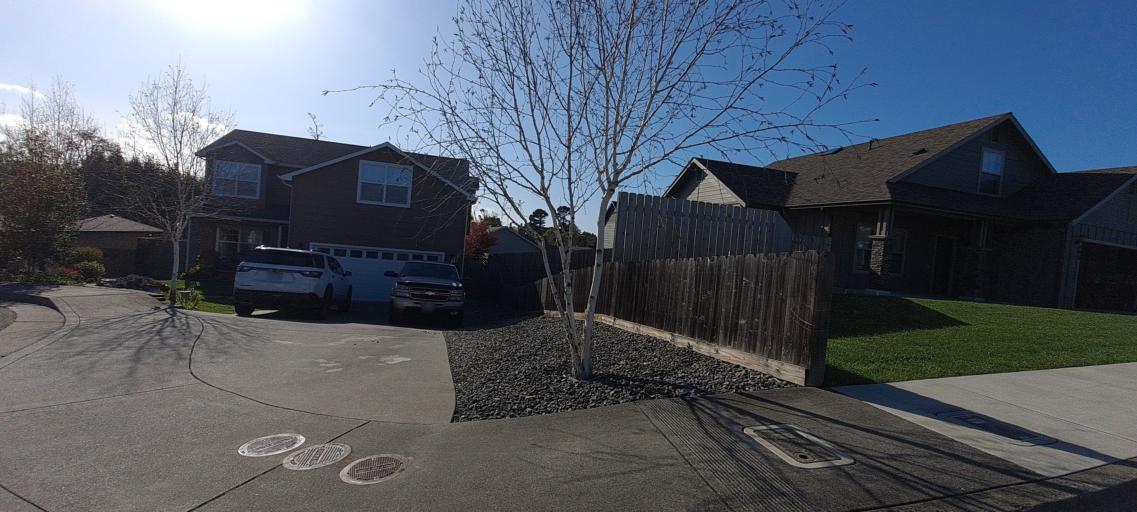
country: US
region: California
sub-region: Humboldt County
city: Fortuna
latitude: 40.5733
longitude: -124.1343
